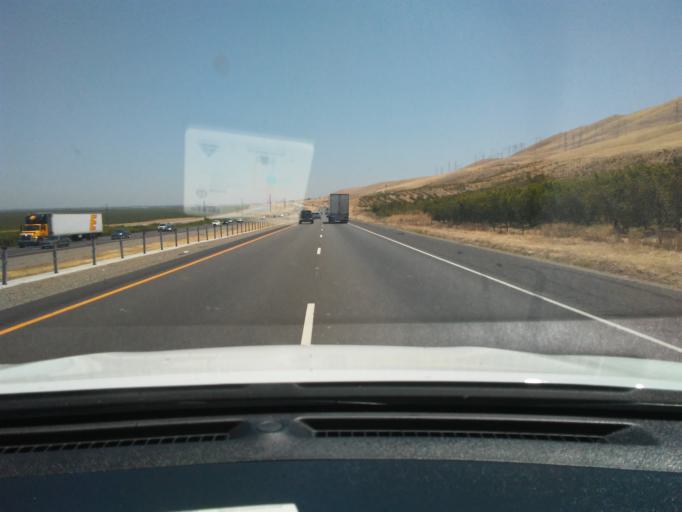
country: US
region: California
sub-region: Stanislaus County
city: Patterson
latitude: 37.5109
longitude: -121.2328
